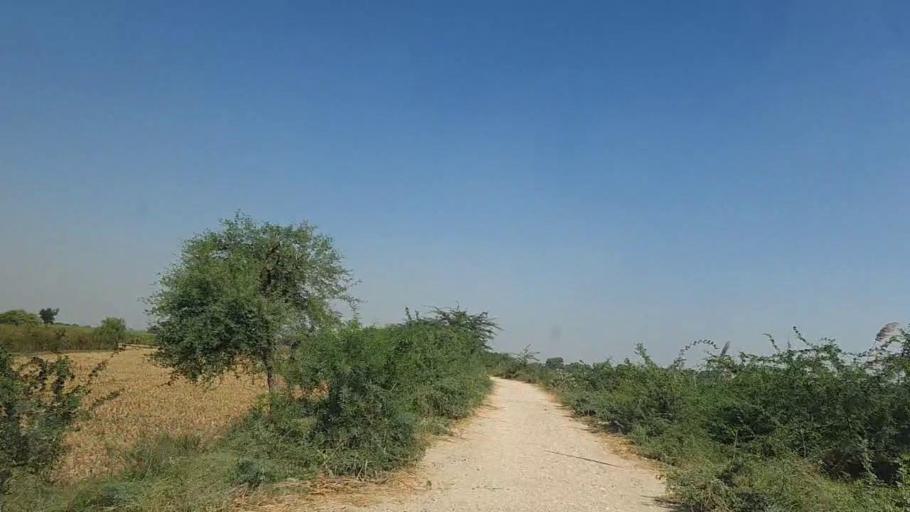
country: PK
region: Sindh
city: Daro Mehar
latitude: 24.8106
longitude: 68.1856
